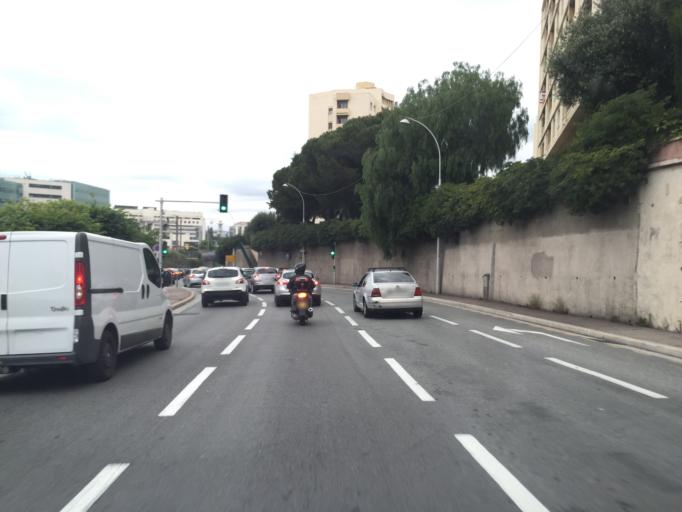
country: FR
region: Provence-Alpes-Cote d'Azur
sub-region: Departement des Alpes-Maritimes
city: Saint-Laurent-du-Var
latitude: 43.6711
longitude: 7.2164
